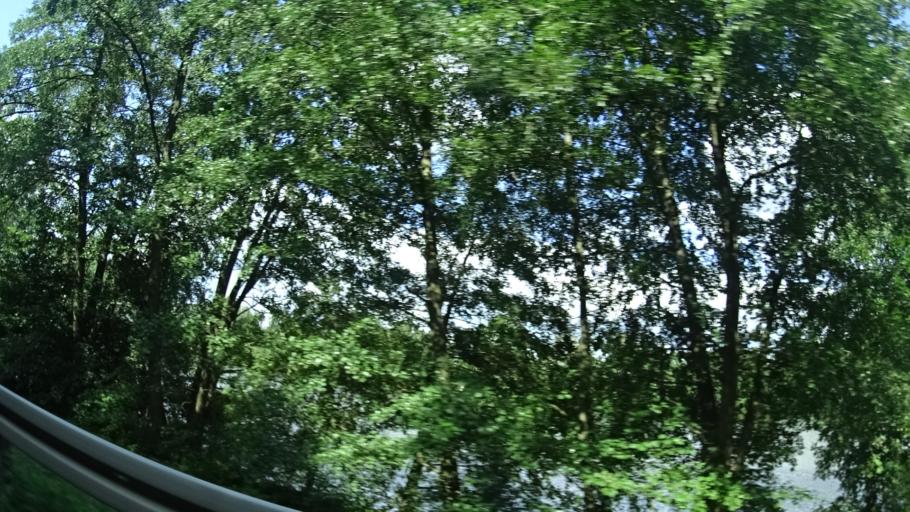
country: DE
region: Bavaria
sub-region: Regierungsbezirk Unterfranken
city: Eltmann
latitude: 49.9752
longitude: 10.6511
